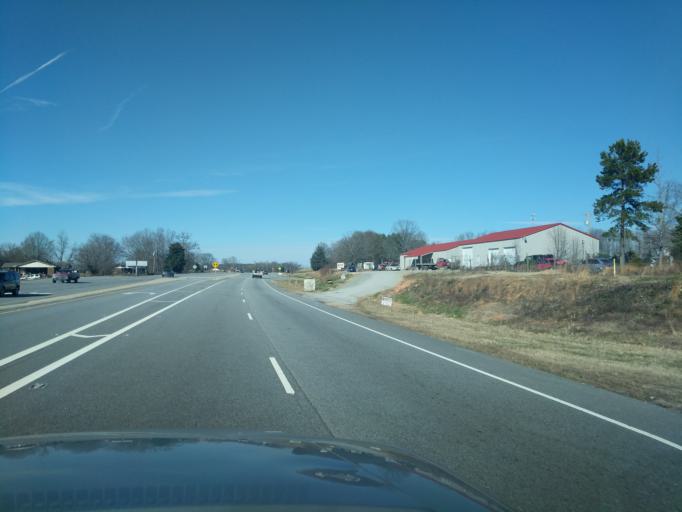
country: US
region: North Carolina
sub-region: Rutherford County
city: Forest City
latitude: 35.2690
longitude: -81.8906
